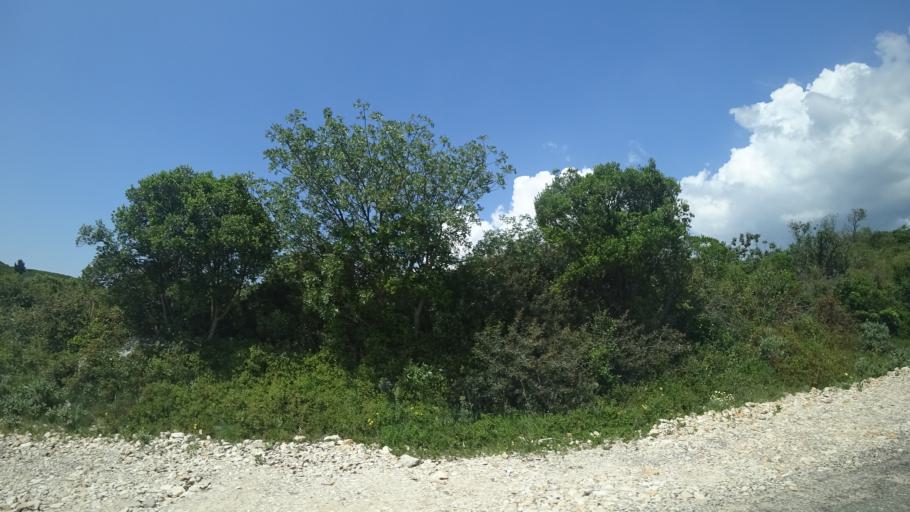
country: FR
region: Languedoc-Roussillon
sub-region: Departement de l'Herault
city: Olonzac
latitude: 43.3535
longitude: 2.7388
